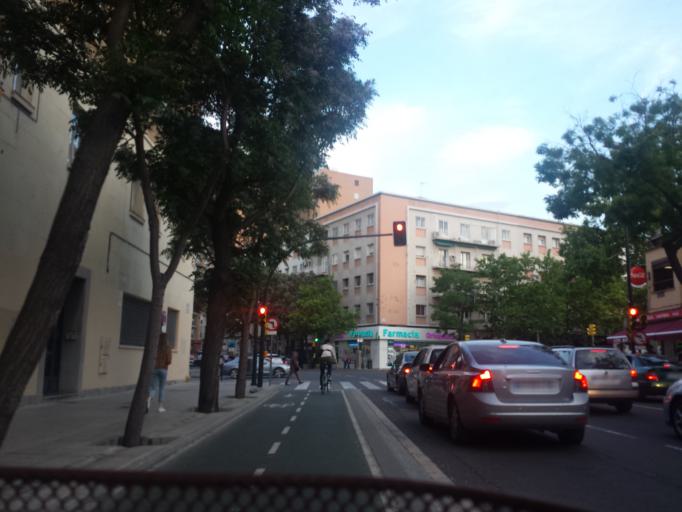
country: ES
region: Aragon
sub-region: Provincia de Zaragoza
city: Delicias
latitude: 41.6455
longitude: -0.9002
